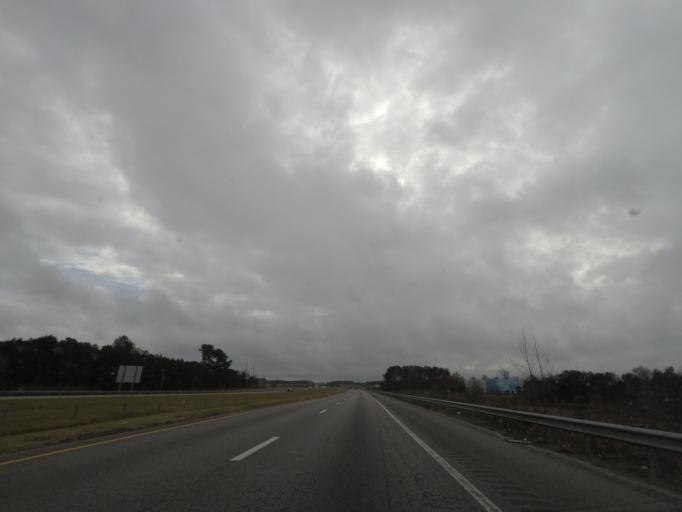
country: US
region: South Carolina
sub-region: Orangeburg County
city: Holly Hill
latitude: 33.4715
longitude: -80.4763
